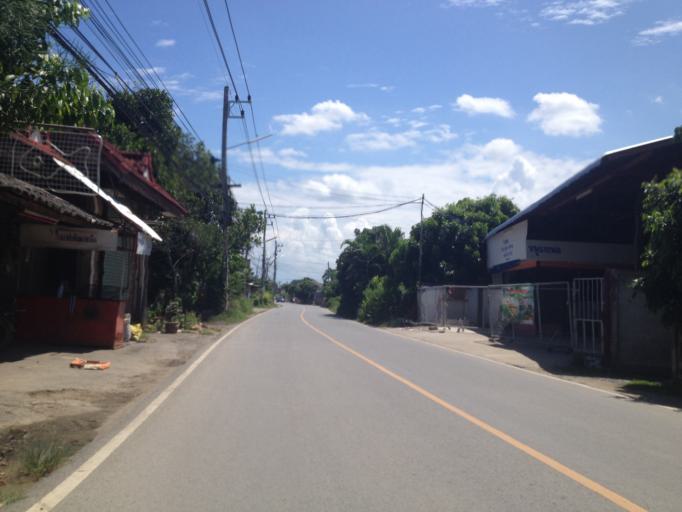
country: TH
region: Chiang Mai
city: Hang Dong
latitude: 18.6561
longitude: 98.9224
